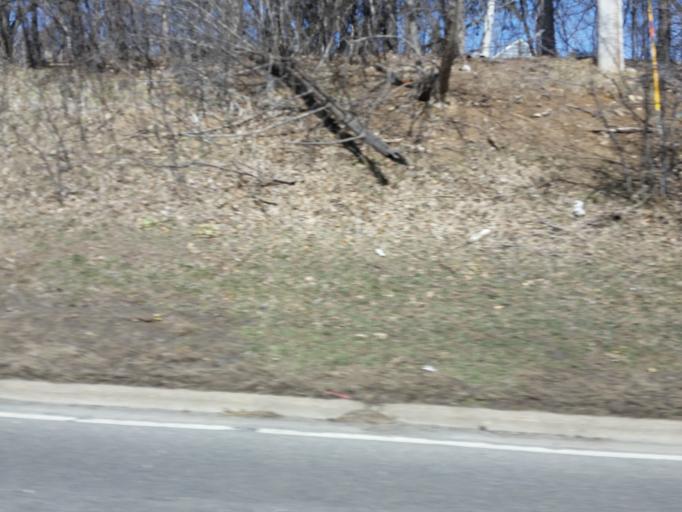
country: US
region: Minnesota
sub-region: Dakota County
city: Eagan
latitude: 44.7901
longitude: -93.1891
